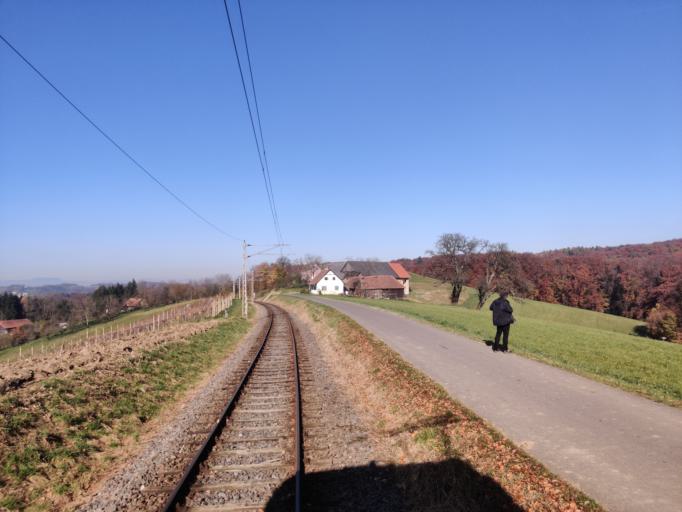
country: AT
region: Styria
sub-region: Politischer Bezirk Suedoststeiermark
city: Maierdorf
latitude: 46.8955
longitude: 15.8341
